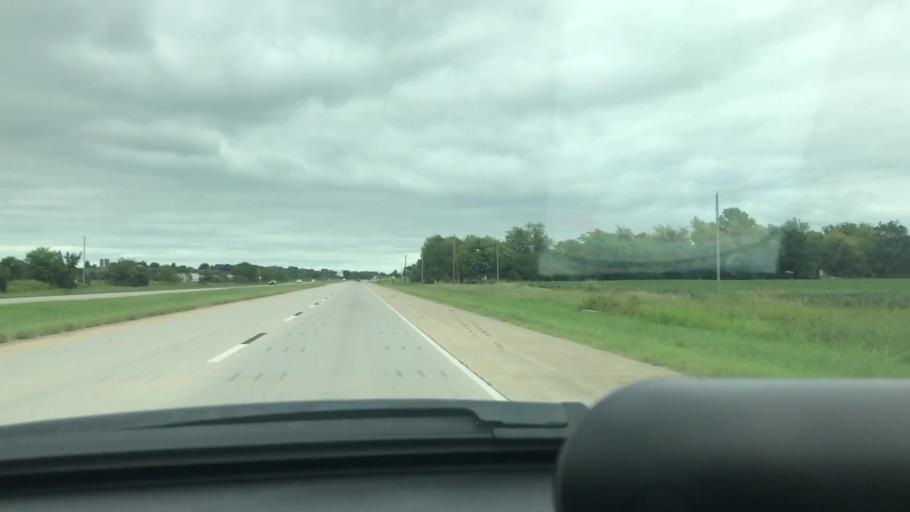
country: US
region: Oklahoma
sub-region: Mayes County
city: Chouteau
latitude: 36.0913
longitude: -95.3634
